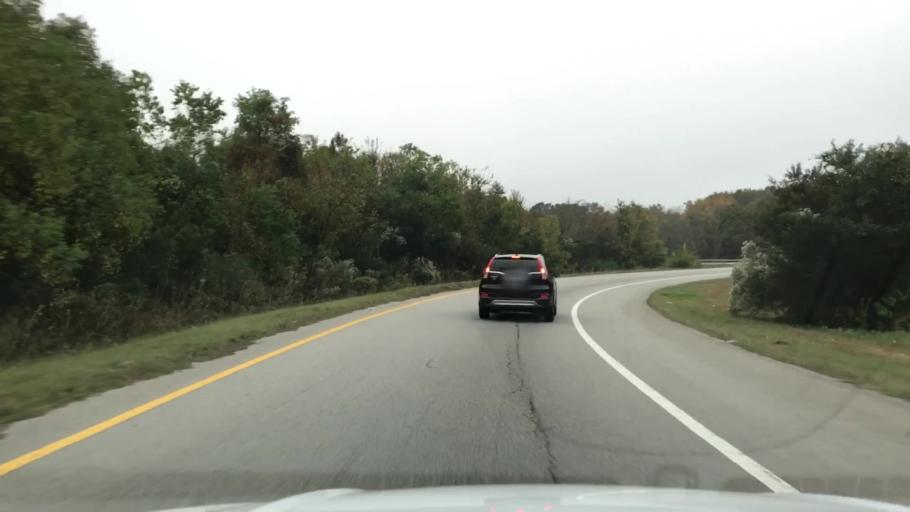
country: US
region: South Carolina
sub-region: Charleston County
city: Shell Point
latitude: 32.8110
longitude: -80.0366
